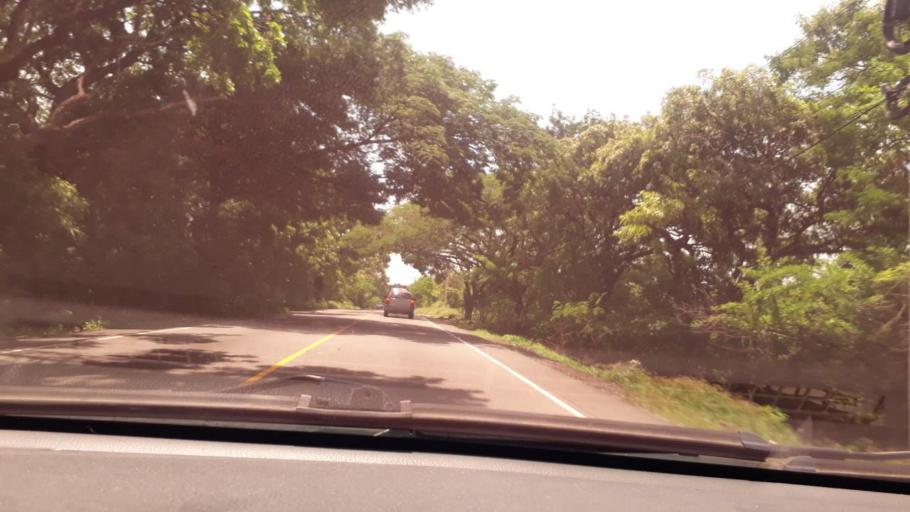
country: GT
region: Zacapa
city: Rio Hondo
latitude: 15.0536
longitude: -89.5596
